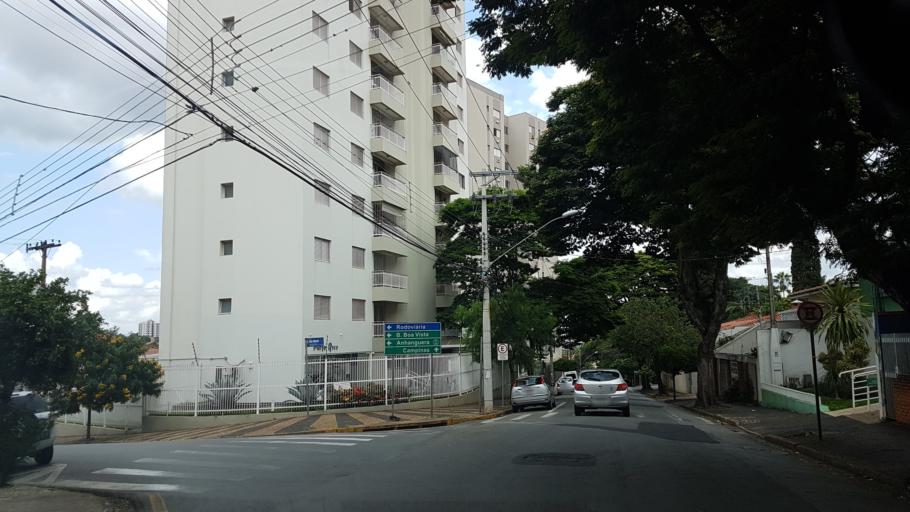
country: BR
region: Sao Paulo
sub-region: Limeira
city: Limeira
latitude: -22.5663
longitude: -47.4009
